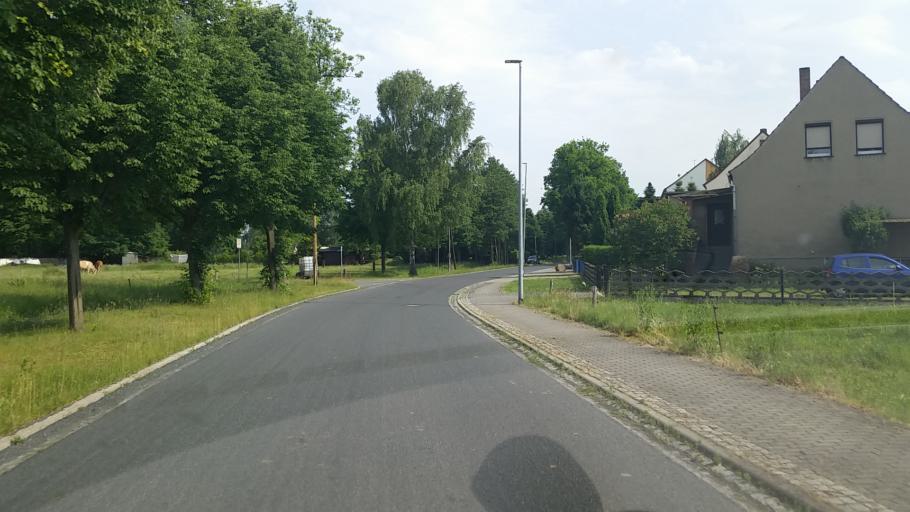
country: DE
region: Brandenburg
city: Hermsdorf
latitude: 51.4029
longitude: 13.8993
